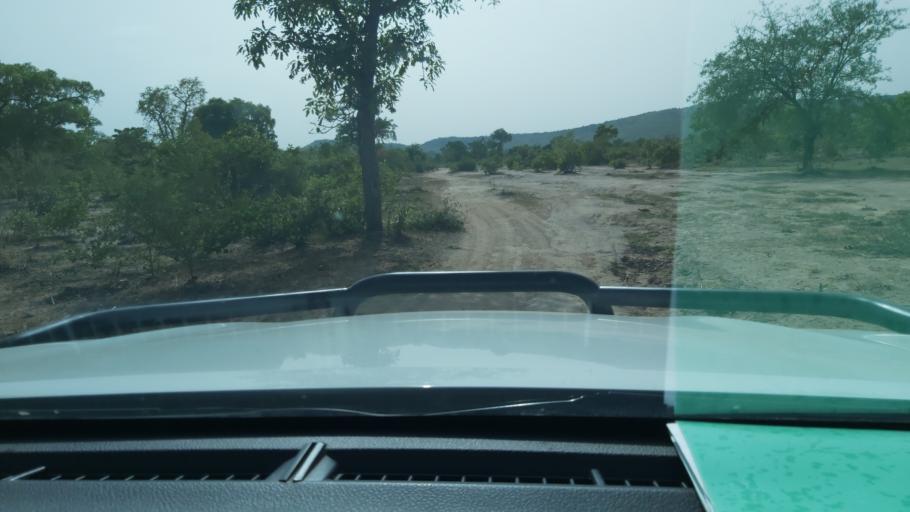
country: ML
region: Koulikoro
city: Koulikoro
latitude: 13.1751
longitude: -7.7407
